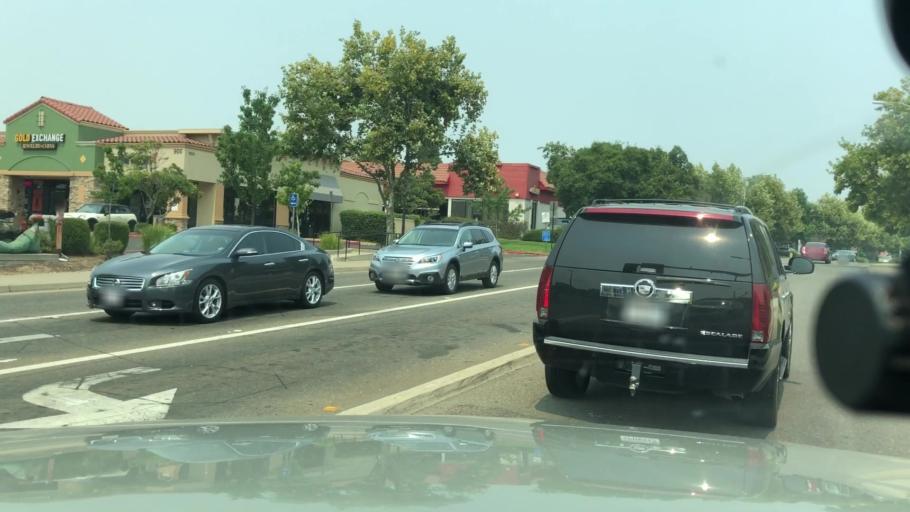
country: US
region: California
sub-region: Sacramento County
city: Folsom
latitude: 38.6704
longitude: -121.1564
